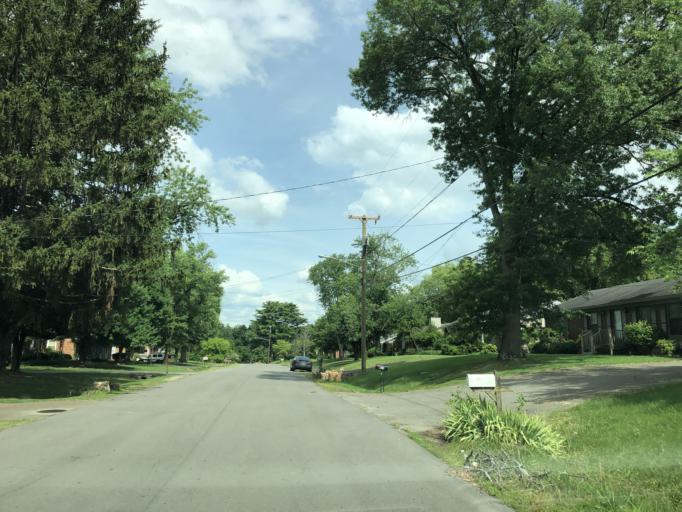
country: US
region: Tennessee
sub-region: Davidson County
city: Oak Hill
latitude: 36.0790
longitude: -86.7422
